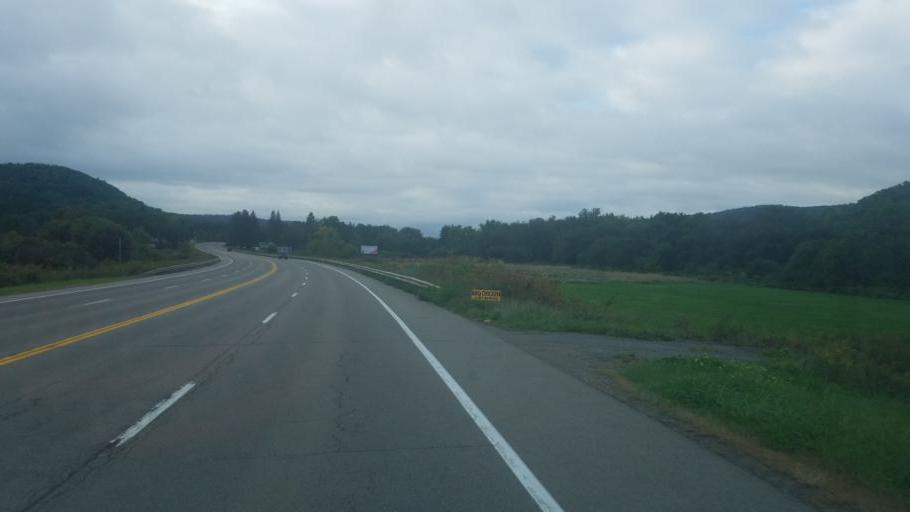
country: US
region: New York
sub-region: Cattaraugus County
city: Weston Mills
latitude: 42.1612
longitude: -78.3971
